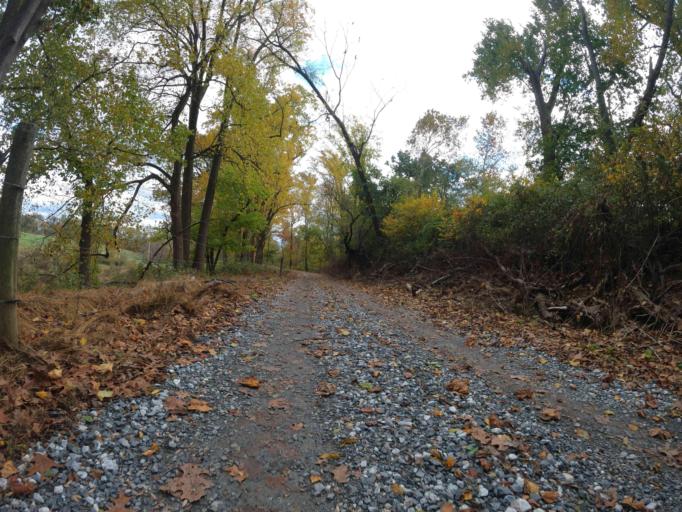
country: US
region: Maryland
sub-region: Carroll County
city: Mount Airy
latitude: 39.3721
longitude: -77.1385
